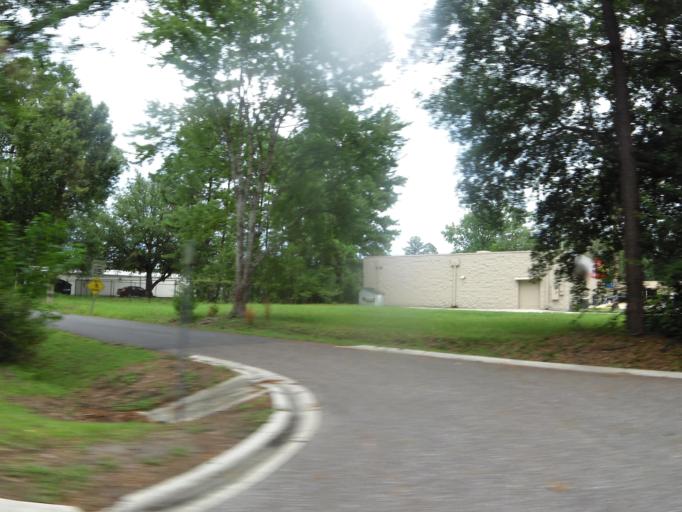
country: US
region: Florida
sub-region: Nassau County
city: Callahan
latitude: 30.5562
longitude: -81.8253
